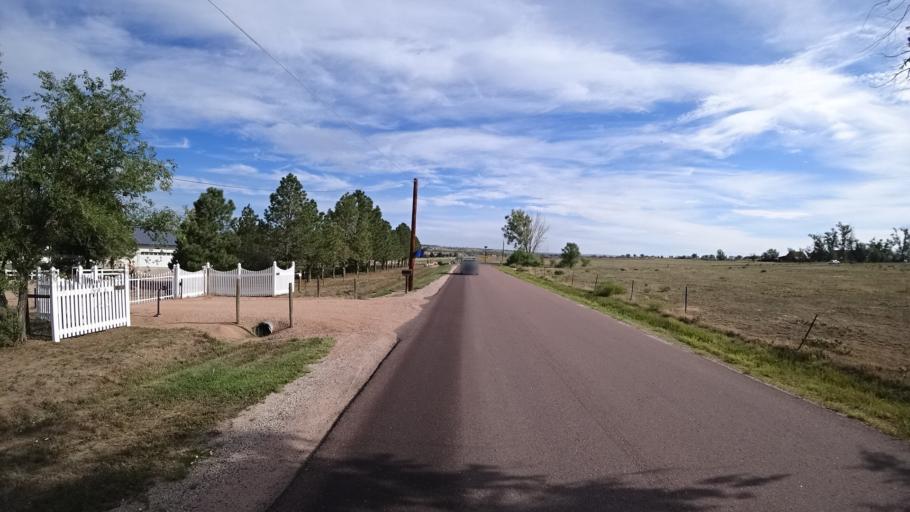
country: US
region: Colorado
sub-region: El Paso County
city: Fountain
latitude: 38.6853
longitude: -104.6782
